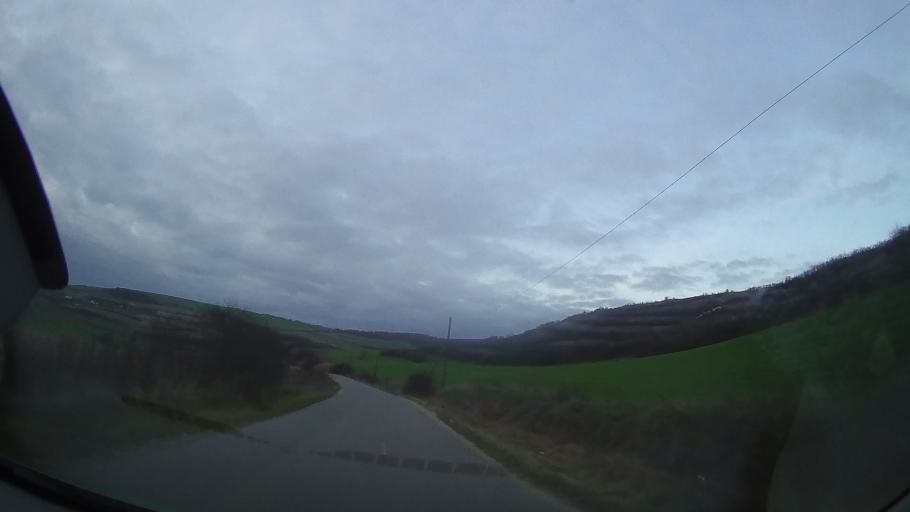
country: RO
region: Cluj
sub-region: Comuna Caianu
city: Vaida-Camaras
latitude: 46.8315
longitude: 23.9678
